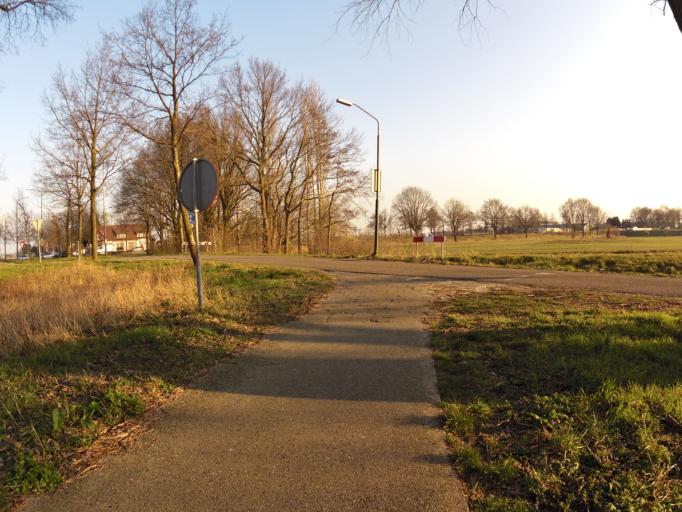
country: NL
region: North Brabant
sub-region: Gemeente Sint-Michielsgestel
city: Sint-Michielsgestel
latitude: 51.6905
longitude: 5.3738
